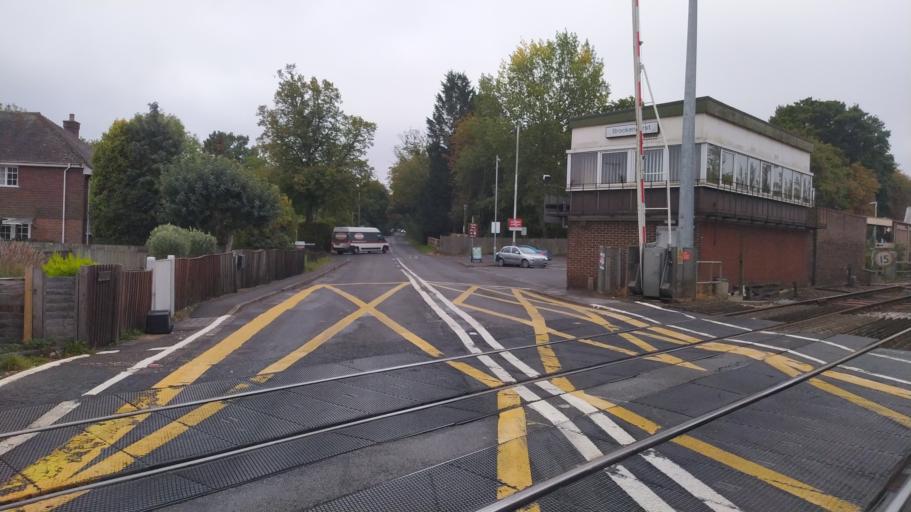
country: GB
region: England
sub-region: Hampshire
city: Brockenhurst
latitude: 50.8178
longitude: -1.5720
